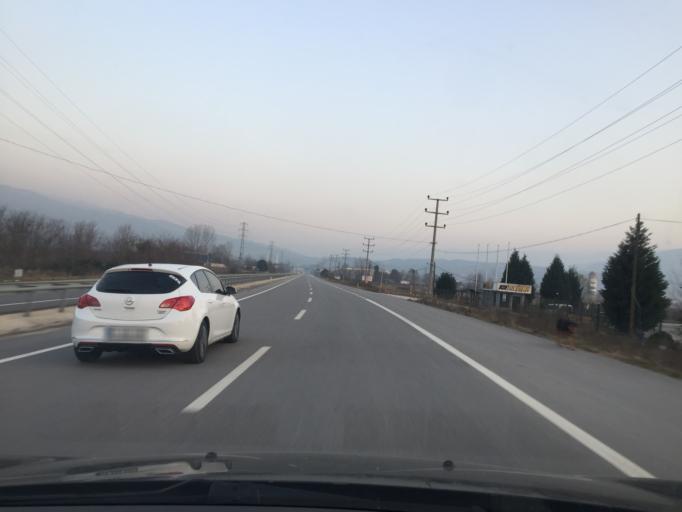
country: TR
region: Sakarya
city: Akyazi
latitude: 40.6402
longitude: 30.6153
